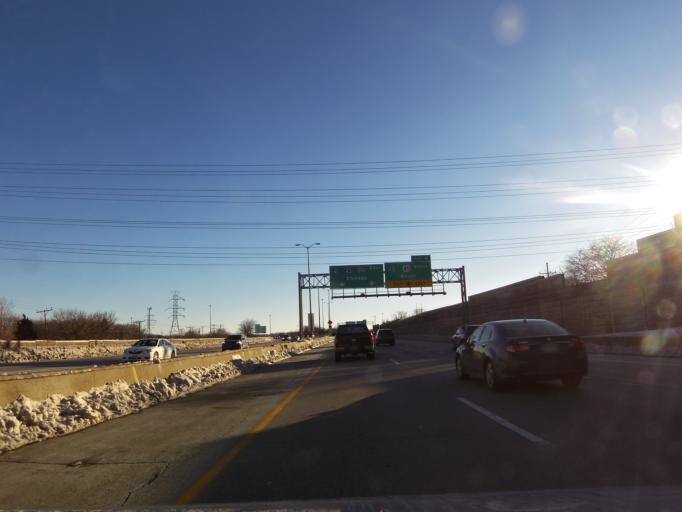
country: US
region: Wisconsin
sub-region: Milwaukee County
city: Greenfield
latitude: 42.9689
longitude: -88.0384
